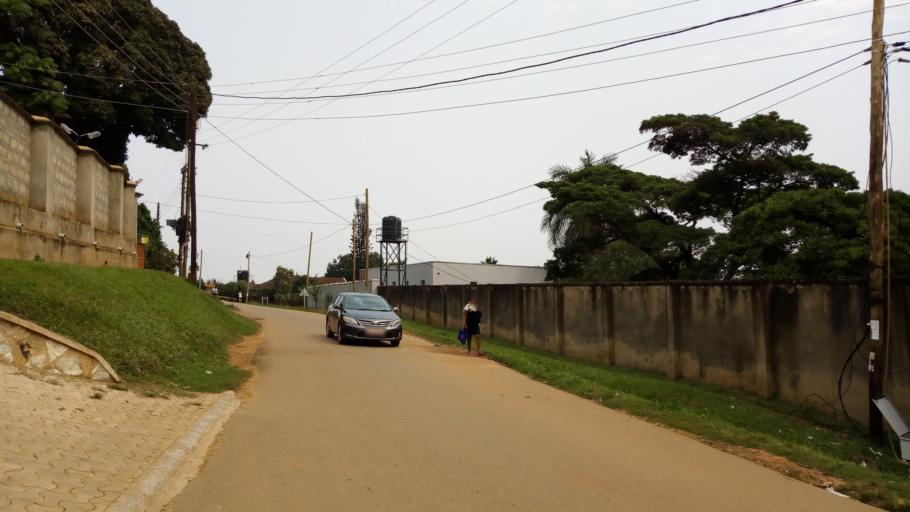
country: UG
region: Central Region
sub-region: Wakiso District
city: Kireka
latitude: 0.3152
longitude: 32.6396
